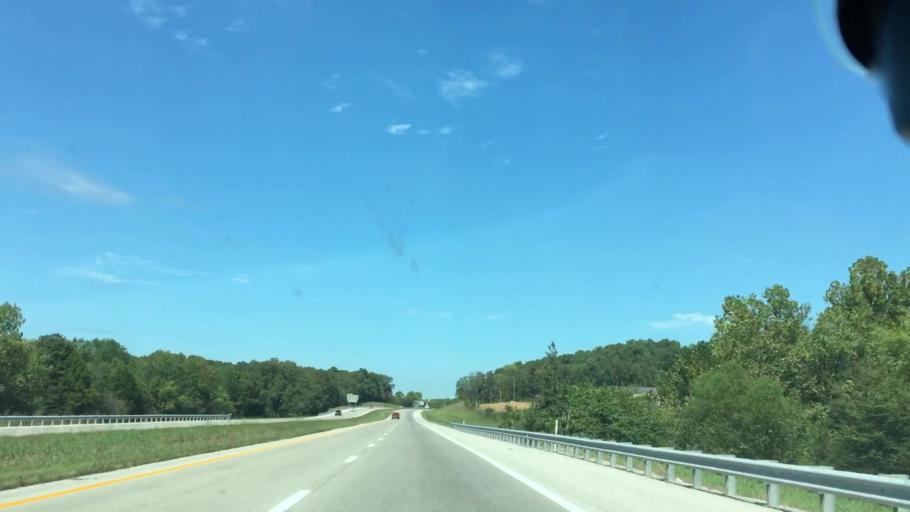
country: US
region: Kentucky
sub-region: Christian County
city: Hopkinsville
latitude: 36.9018
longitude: -87.4708
